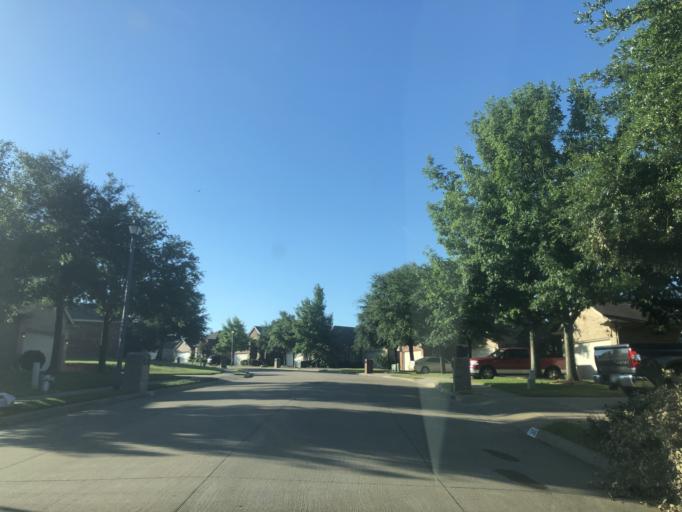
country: US
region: Texas
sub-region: Dallas County
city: Duncanville
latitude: 32.6592
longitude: -96.9485
